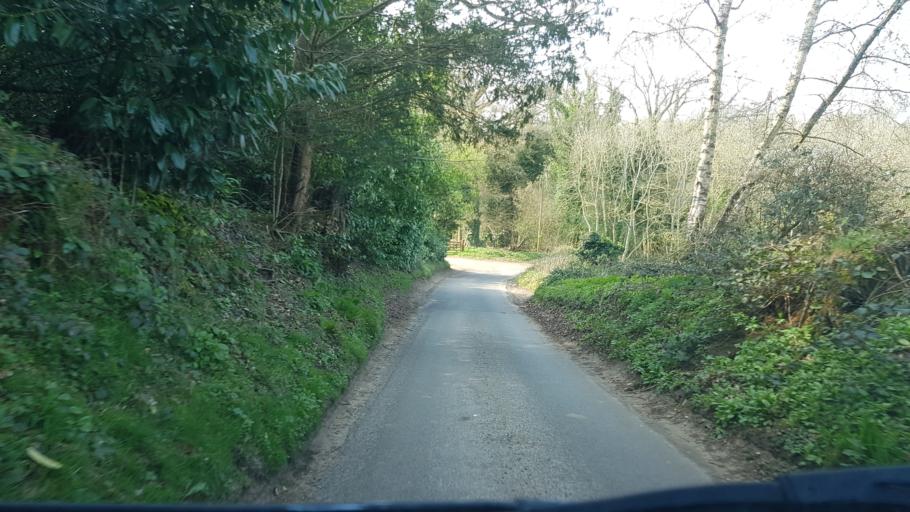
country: GB
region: England
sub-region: Surrey
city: Chilworth
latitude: 51.2271
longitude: -0.5198
